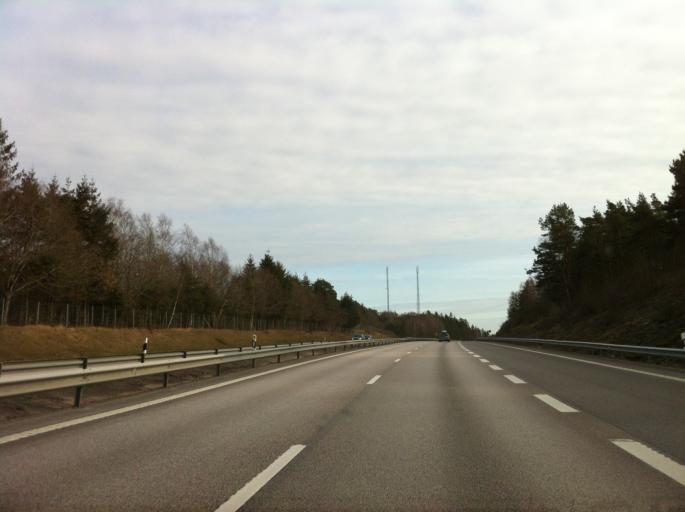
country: SE
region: Halland
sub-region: Kungsbacka Kommun
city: Kungsbacka
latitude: 57.5064
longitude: 12.0525
